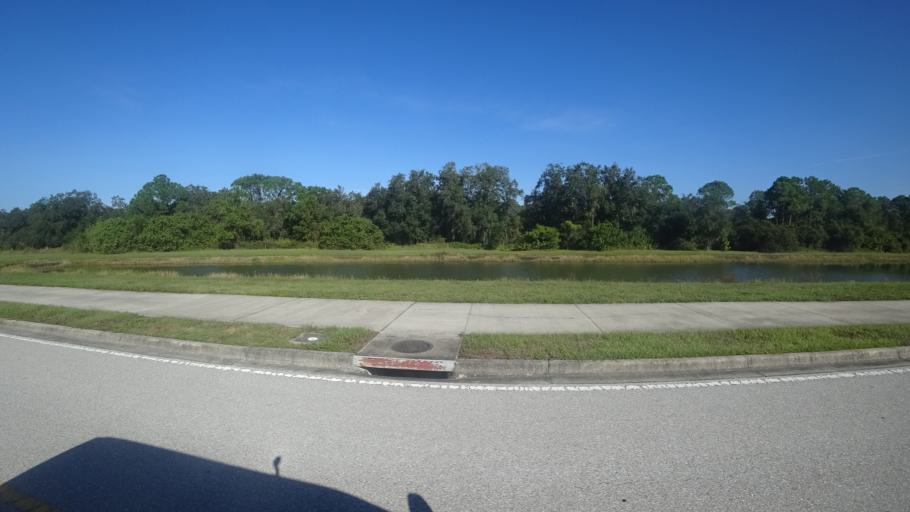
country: US
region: Florida
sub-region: Sarasota County
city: The Meadows
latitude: 27.4209
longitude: -82.4173
